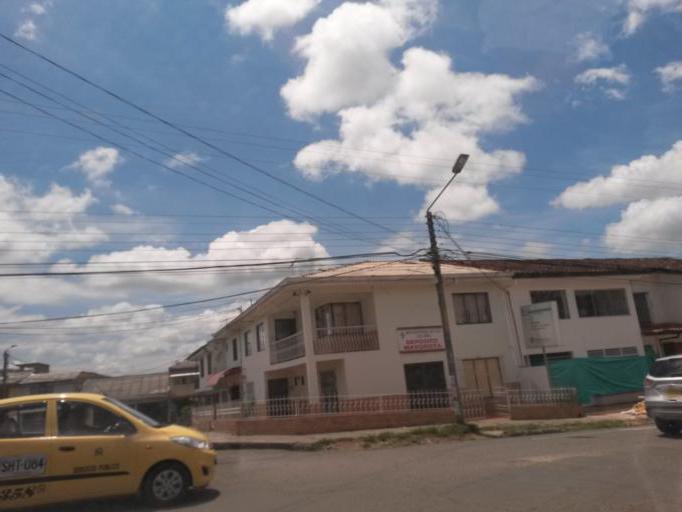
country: CO
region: Cauca
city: Popayan
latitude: 2.4504
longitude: -76.6041
